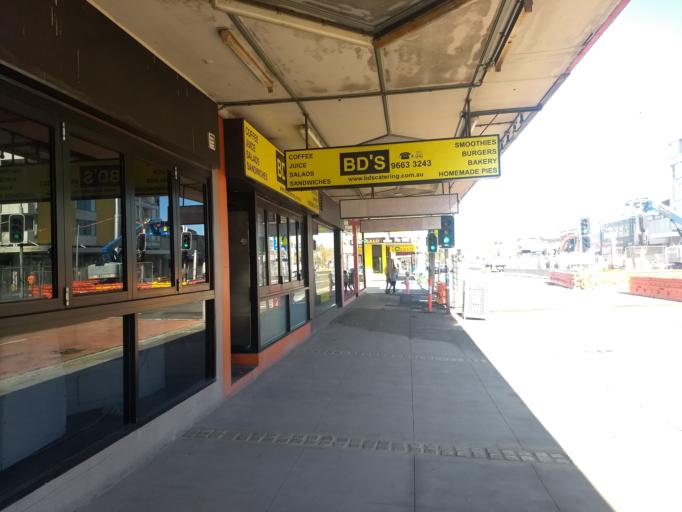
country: AU
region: New South Wales
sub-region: Randwick
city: Kensington
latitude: -33.9086
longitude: 151.2236
